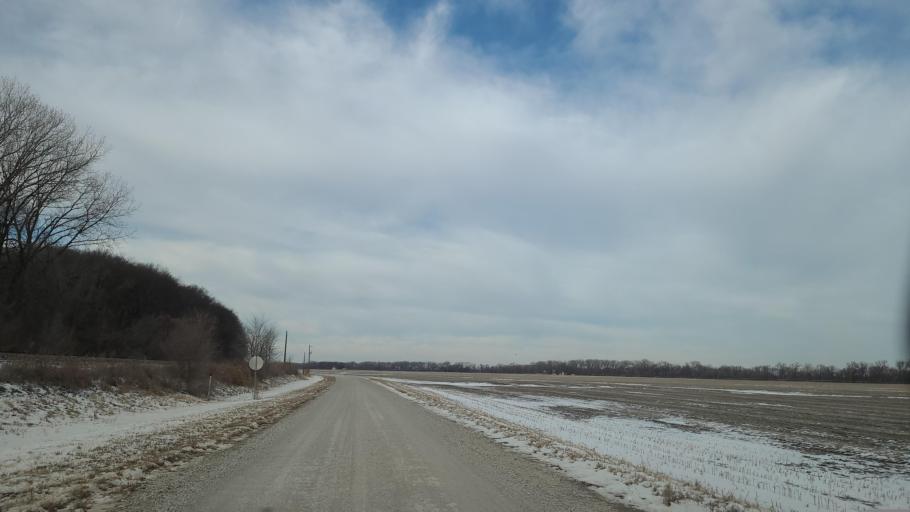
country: US
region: Kansas
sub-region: Jefferson County
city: Oskaloosa
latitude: 39.0610
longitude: -95.4257
